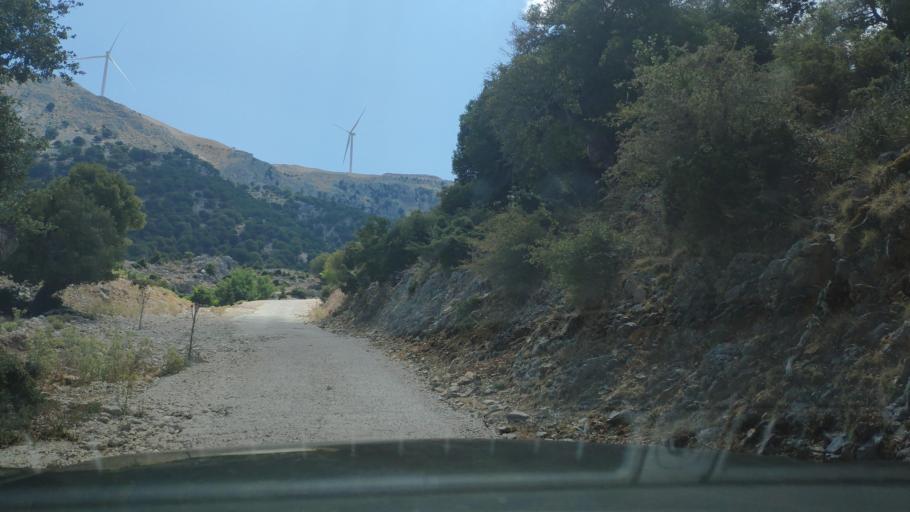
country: GR
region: West Greece
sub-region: Nomos Aitolias kai Akarnanias
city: Monastirakion
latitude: 38.7837
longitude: 20.9831
